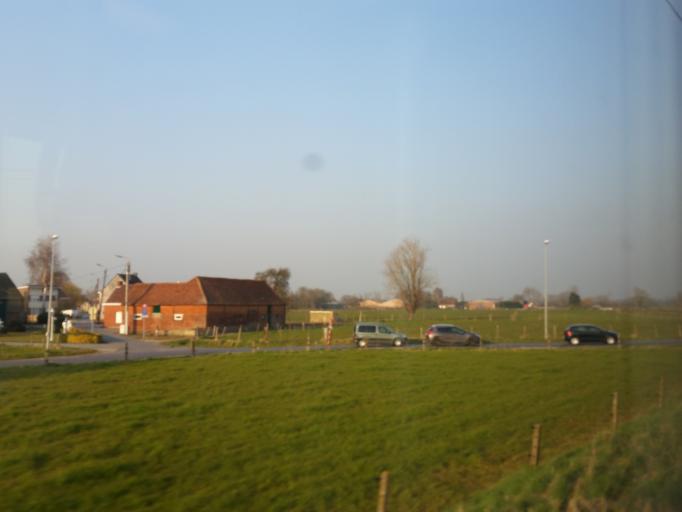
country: BE
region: Flanders
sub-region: Provincie Oost-Vlaanderen
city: Berlare
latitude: 51.0067
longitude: 4.0264
